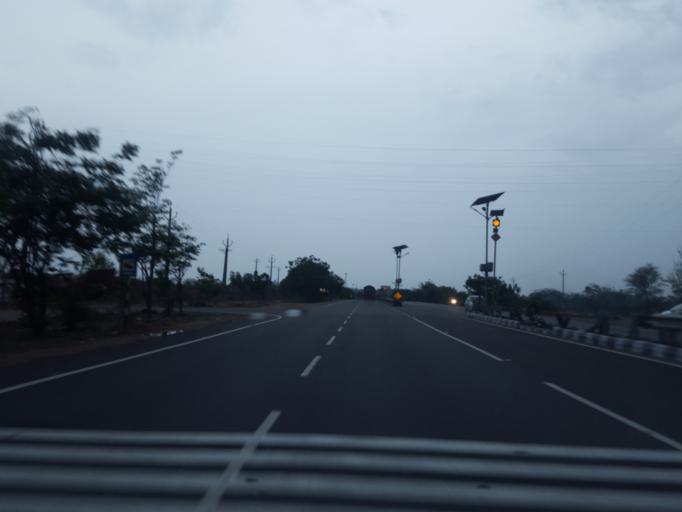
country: IN
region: Telangana
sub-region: Mahbubnagar
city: Farrukhnagar
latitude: 17.1139
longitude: 78.2656
